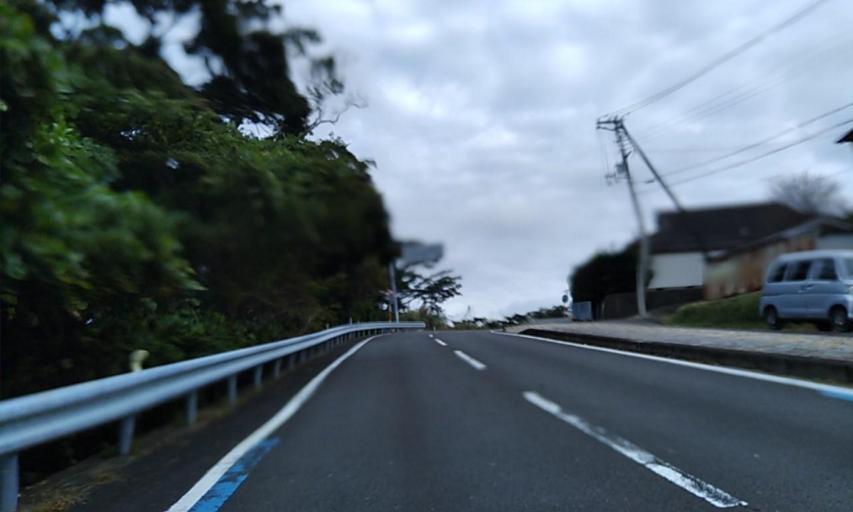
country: JP
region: Wakayama
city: Shingu
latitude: 33.5898
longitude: 135.9520
